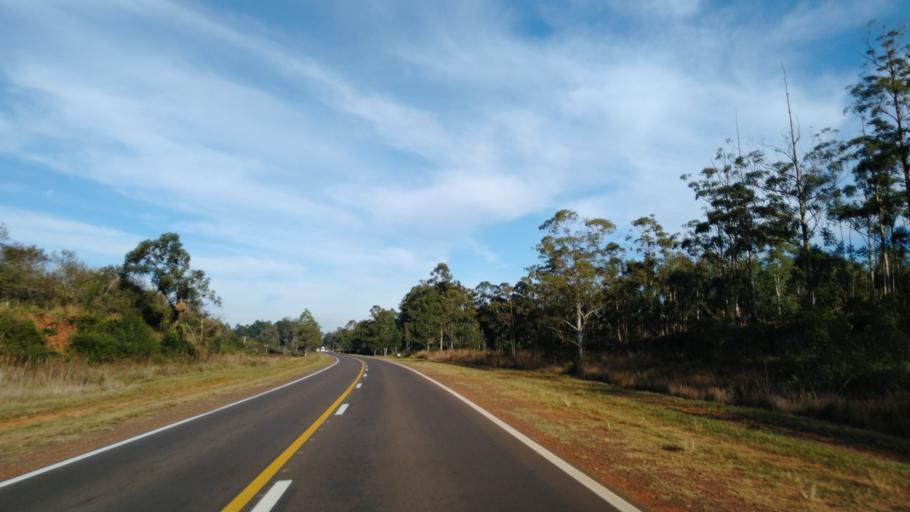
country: AR
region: Corrientes
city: Yapeyu
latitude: -29.4246
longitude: -56.8597
